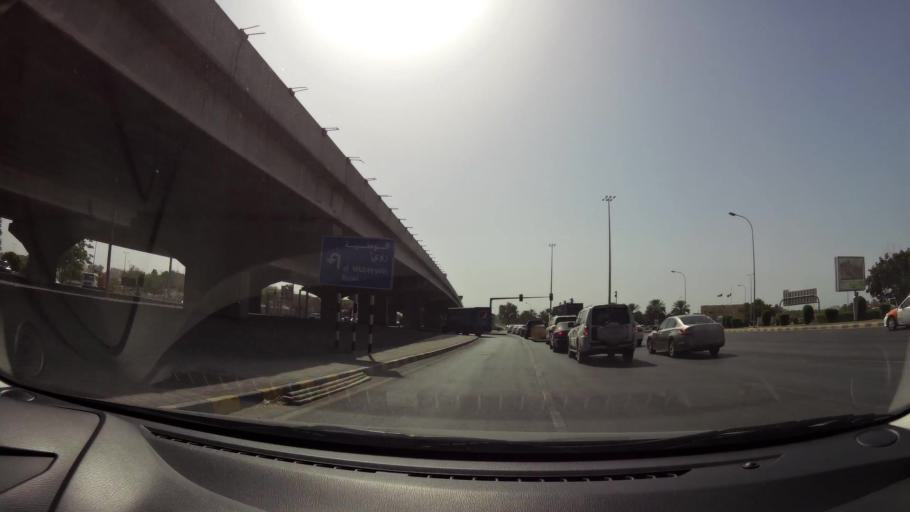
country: OM
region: Muhafazat Masqat
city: Muscat
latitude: 23.6114
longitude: 58.4936
